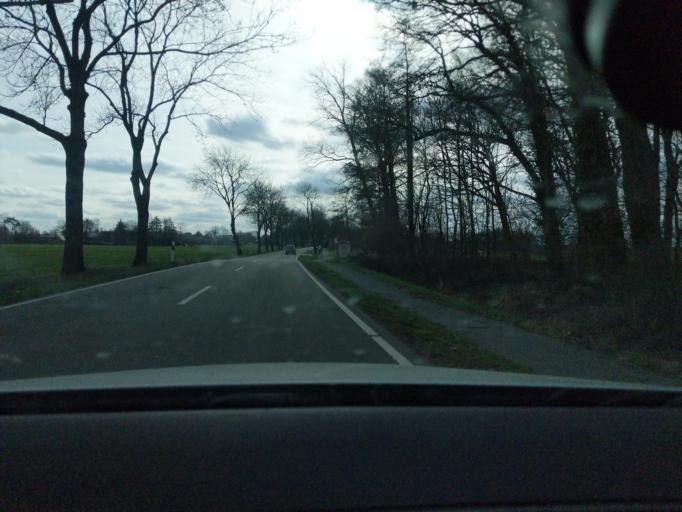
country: DE
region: Lower Saxony
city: Engelschoff
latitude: 53.6484
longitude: 9.3391
